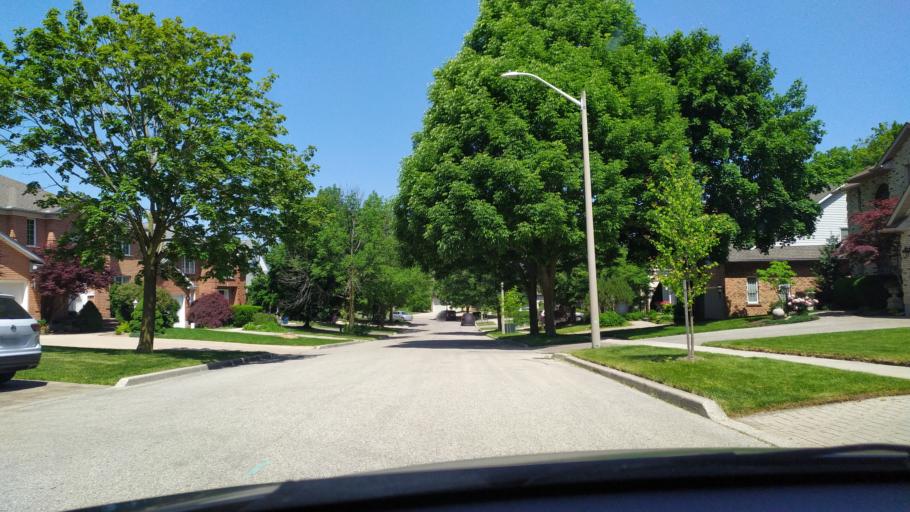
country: CA
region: Ontario
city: Waterloo
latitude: 43.4543
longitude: -80.5680
